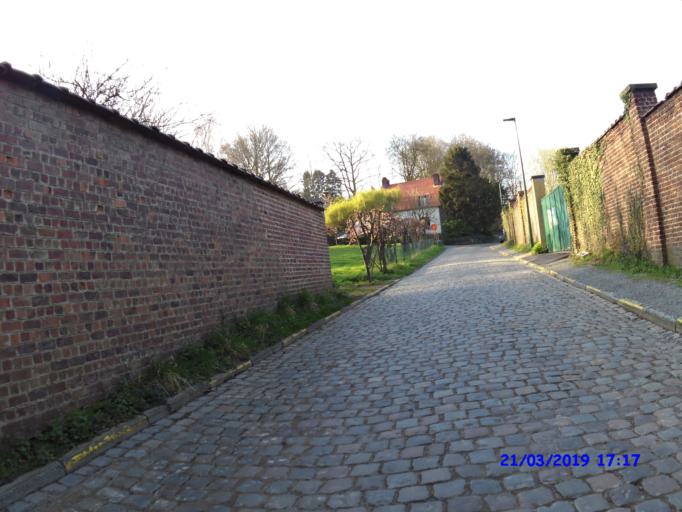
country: BE
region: Flanders
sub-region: Provincie Vlaams-Brabant
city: Sint-Genesius-Rode
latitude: 50.7450
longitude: 4.3429
